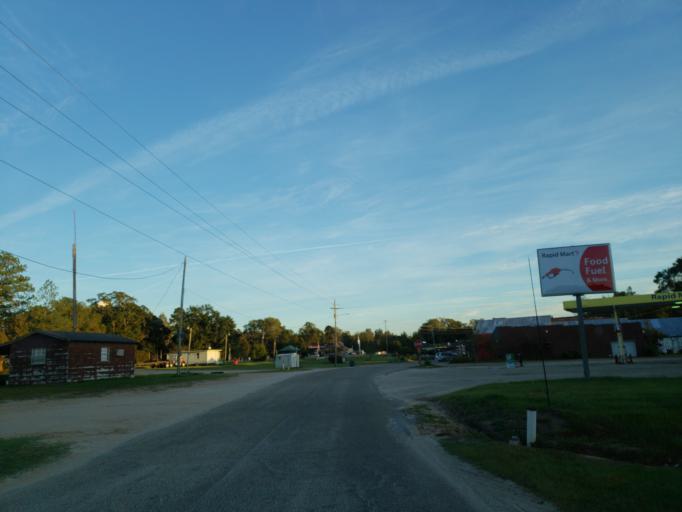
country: US
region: Mississippi
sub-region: Wayne County
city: Belmont
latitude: 31.4368
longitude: -88.4745
